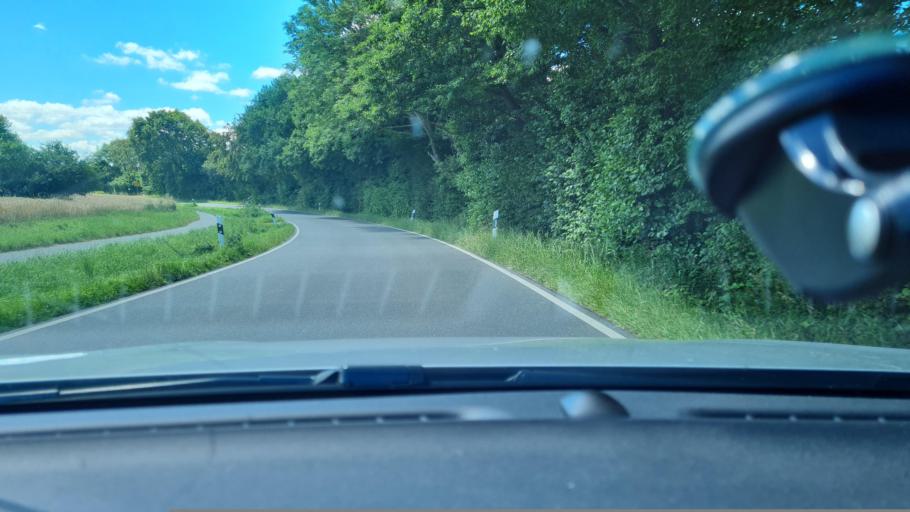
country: DE
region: Schleswig-Holstein
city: Winnemark
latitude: 54.6209
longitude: 9.9300
